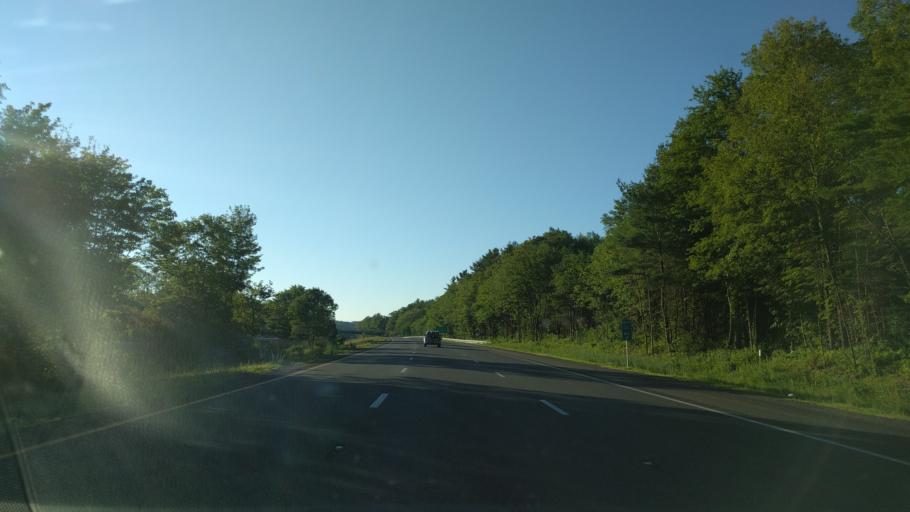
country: US
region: Massachusetts
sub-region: Norfolk County
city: Bellingham
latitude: 42.1058
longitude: -71.4555
